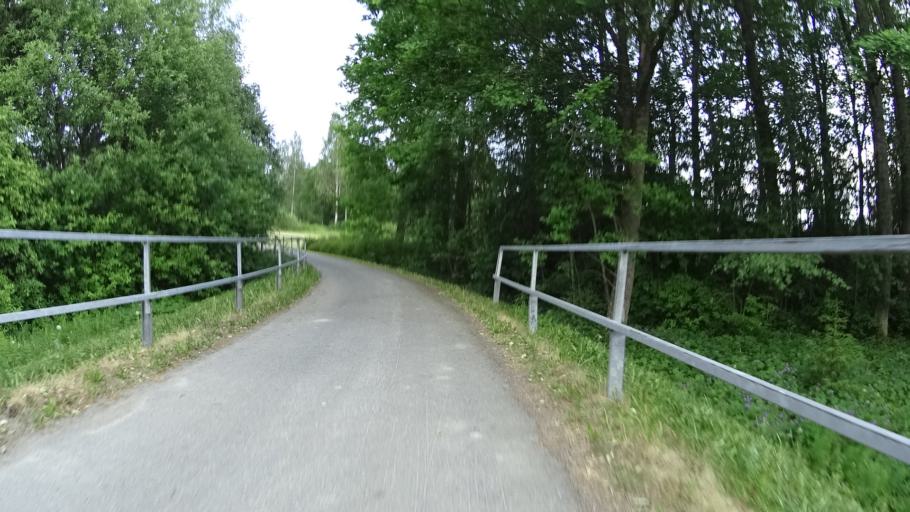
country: FI
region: Uusimaa
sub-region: Raaseporin
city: Karis
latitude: 60.0948
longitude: 23.6267
